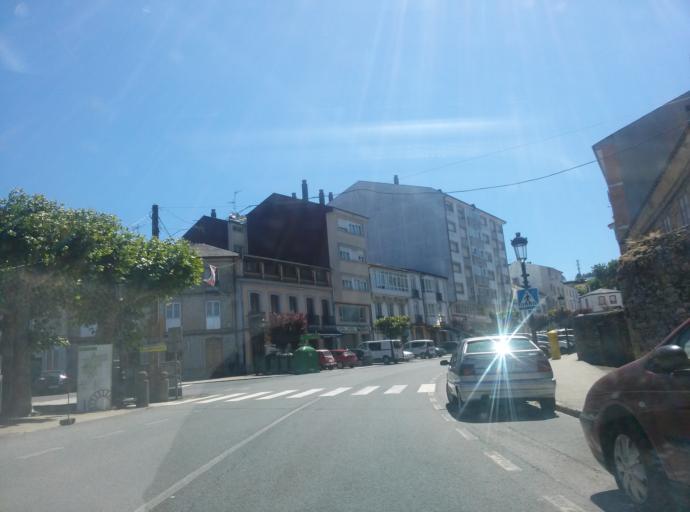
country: ES
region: Galicia
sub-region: Provincia de Lugo
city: Meira
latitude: 43.2137
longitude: -7.2940
